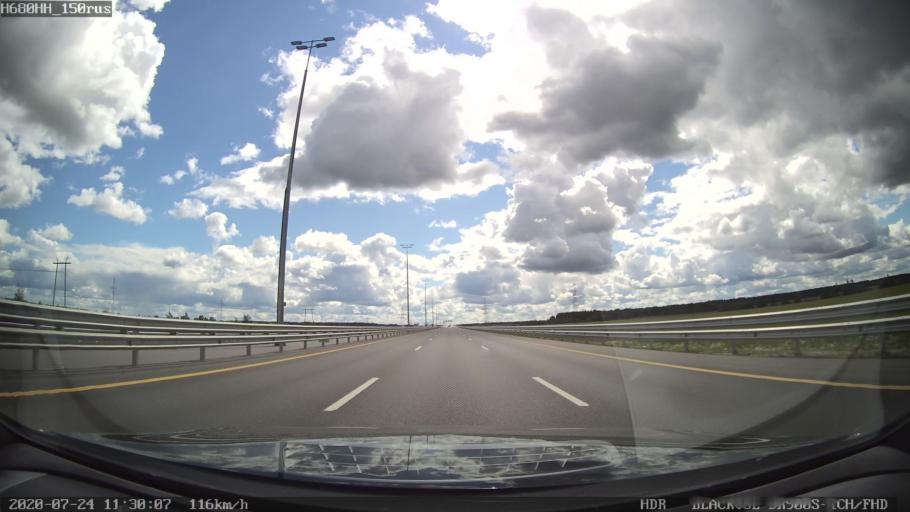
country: RU
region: Leningrad
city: Krasnyy Bor
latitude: 59.6731
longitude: 30.6058
